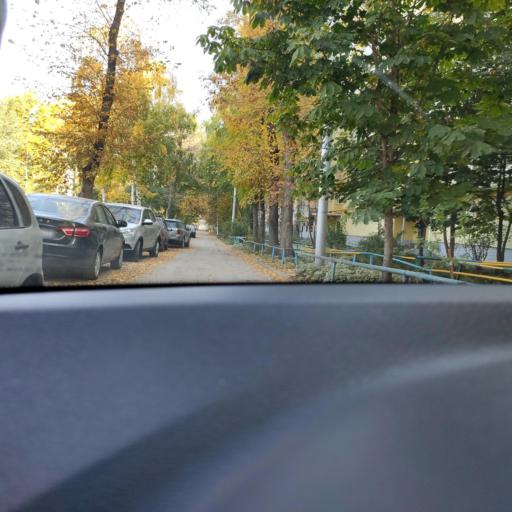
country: RU
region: Samara
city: Petra-Dubrava
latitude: 53.2435
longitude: 50.2614
